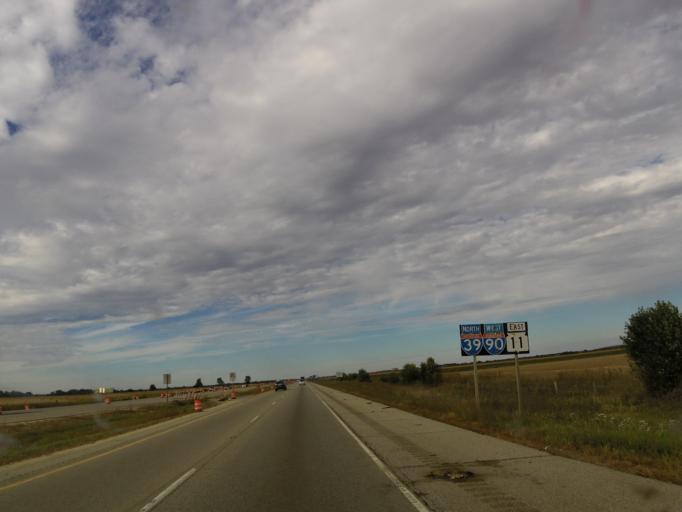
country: US
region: Wisconsin
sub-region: Rock County
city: Janesville
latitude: 42.6431
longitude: -88.9829
